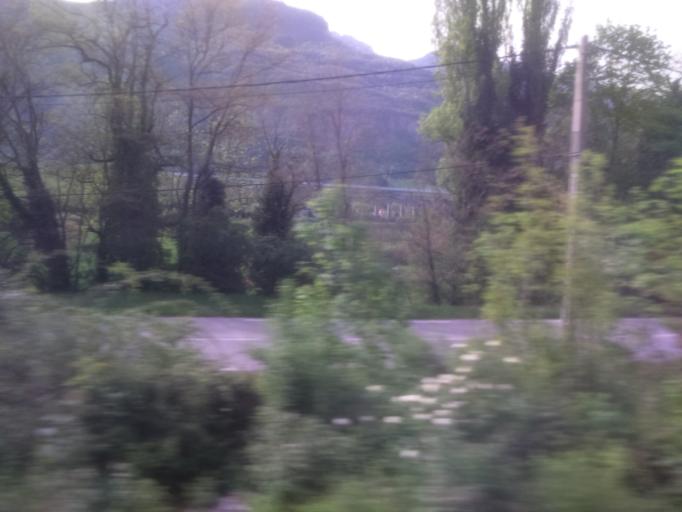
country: FR
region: Rhone-Alpes
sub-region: Departement de l'Isere
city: Vif
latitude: 45.0382
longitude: 5.6716
